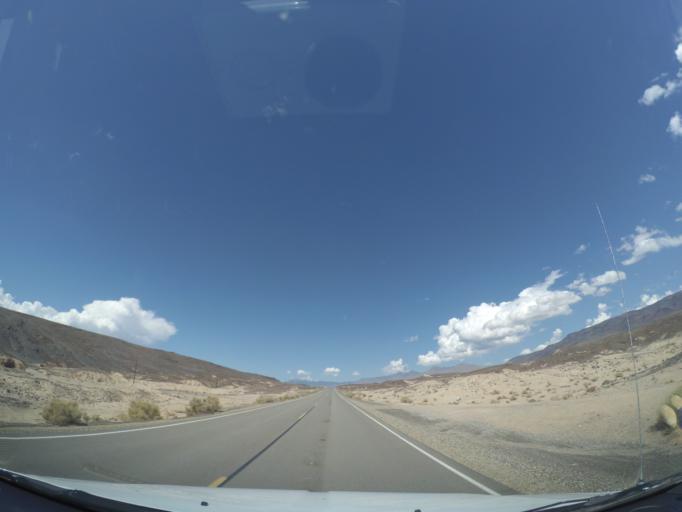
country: US
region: California
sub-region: Inyo County
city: Lone Pine
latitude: 36.3813
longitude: -117.8041
